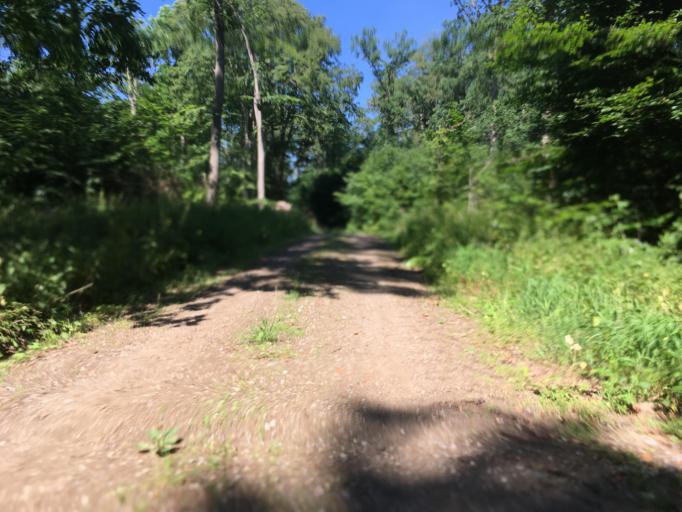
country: DE
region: Brandenburg
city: Marienwerder
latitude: 52.9217
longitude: 13.6208
